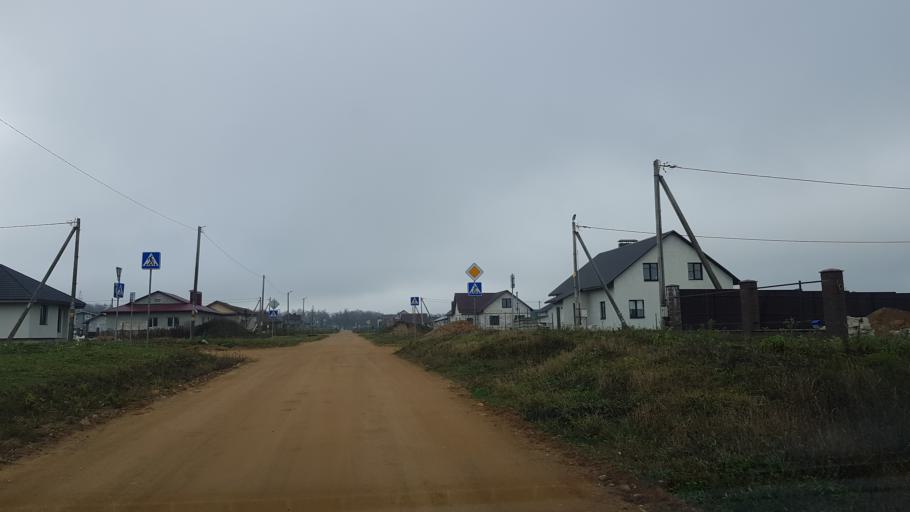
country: BY
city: Fanipol
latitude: 53.7311
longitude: 27.3235
